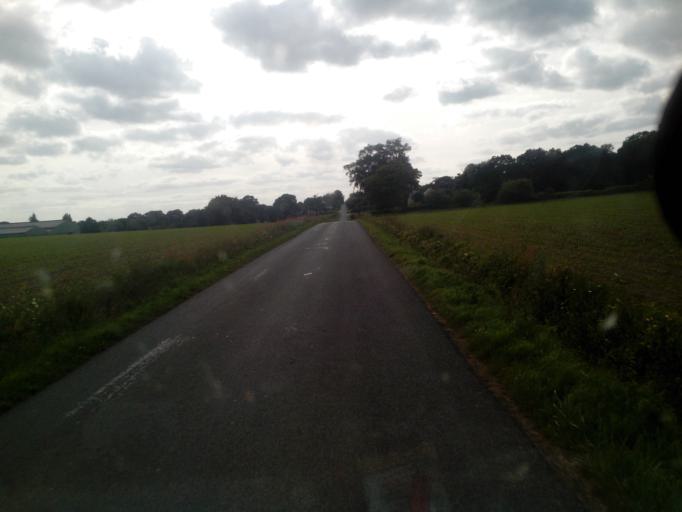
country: FR
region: Brittany
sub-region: Departement d'Ille-et-Vilaine
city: Saint-Medard-sur-Ille
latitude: 48.2475
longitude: -1.6380
